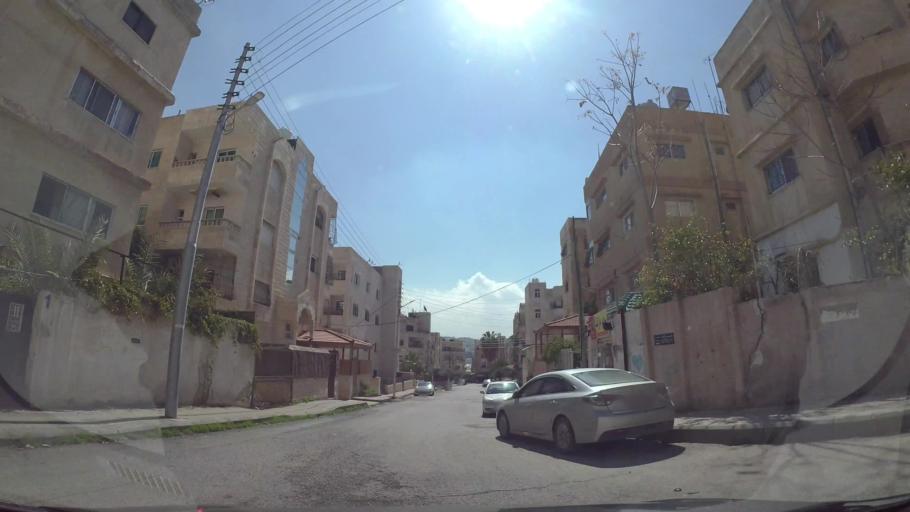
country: JO
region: Amman
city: Amman
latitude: 31.9786
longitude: 35.9938
